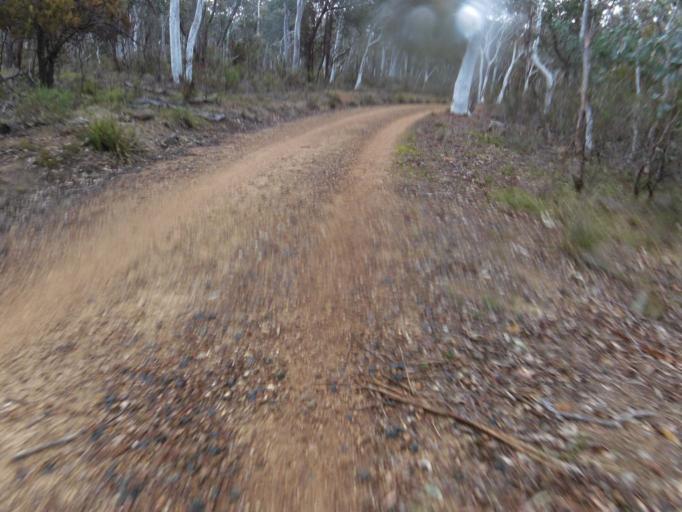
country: AU
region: Australian Capital Territory
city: Acton
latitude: -35.2658
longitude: 149.0935
